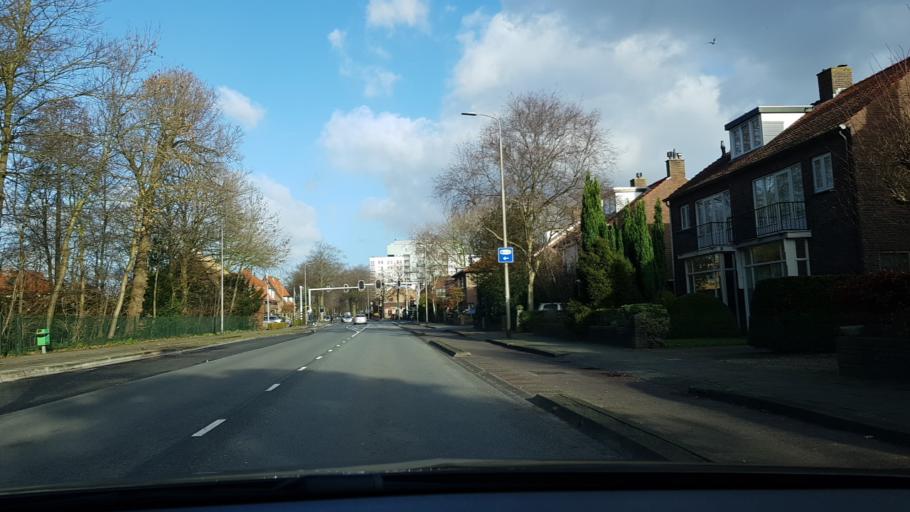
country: NL
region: South Holland
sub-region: Gemeente Teylingen
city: Sassenheim
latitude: 52.2250
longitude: 4.5262
